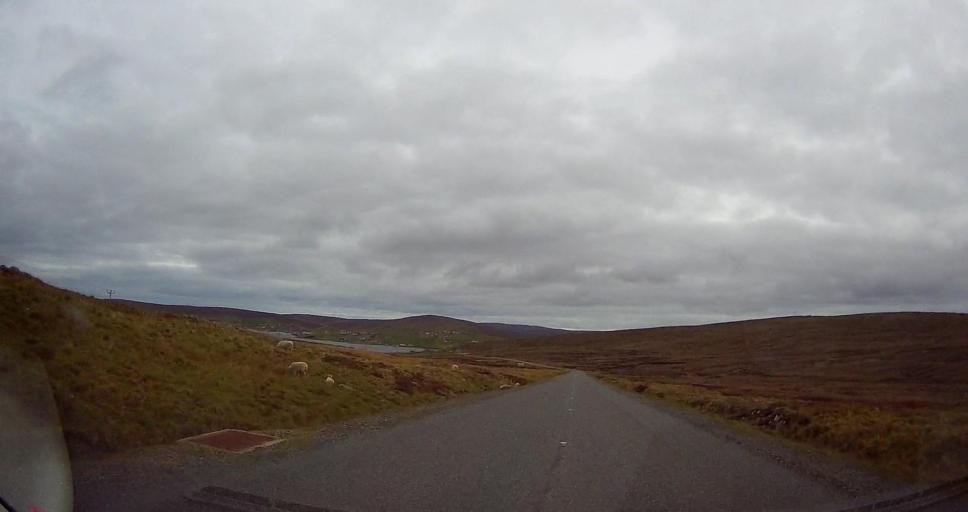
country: GB
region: Scotland
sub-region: Shetland Islands
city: Shetland
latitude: 60.6237
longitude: -1.0735
